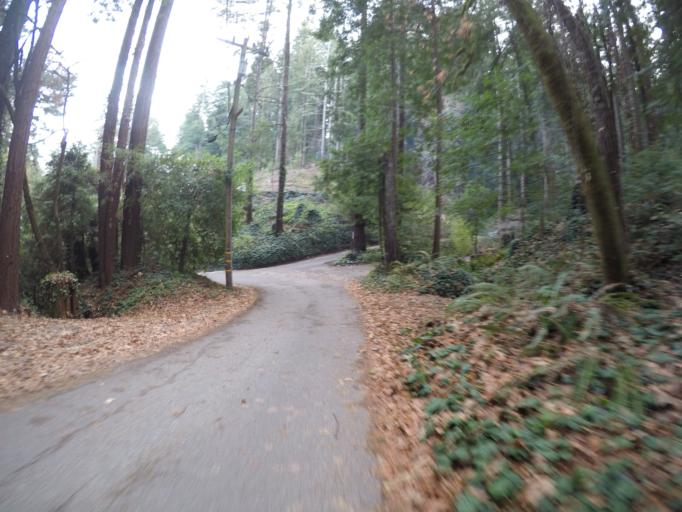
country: US
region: California
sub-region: Santa Cruz County
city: Mount Hermon
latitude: 37.0650
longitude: -122.0380
